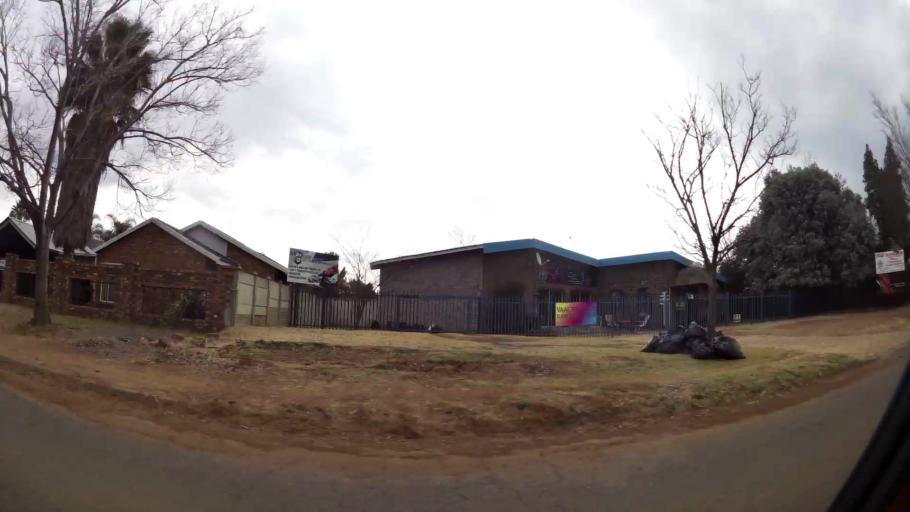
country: ZA
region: Gauteng
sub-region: Sedibeng District Municipality
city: Vanderbijlpark
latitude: -26.7130
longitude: 27.8243
